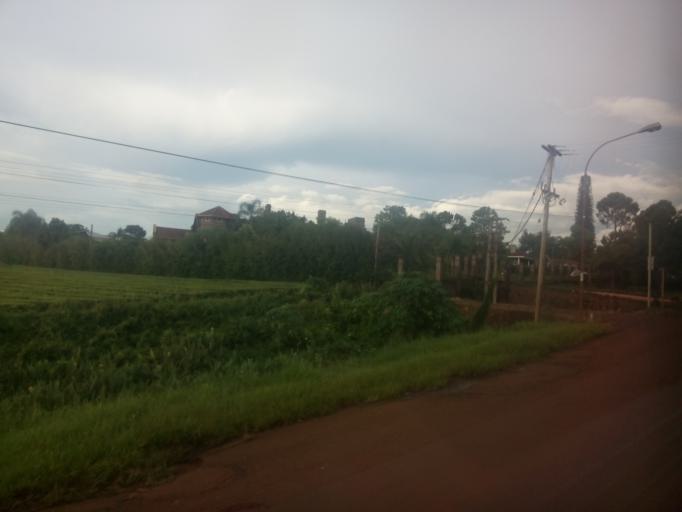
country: AR
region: Misiones
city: Guarani
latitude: -27.4911
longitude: -55.1519
